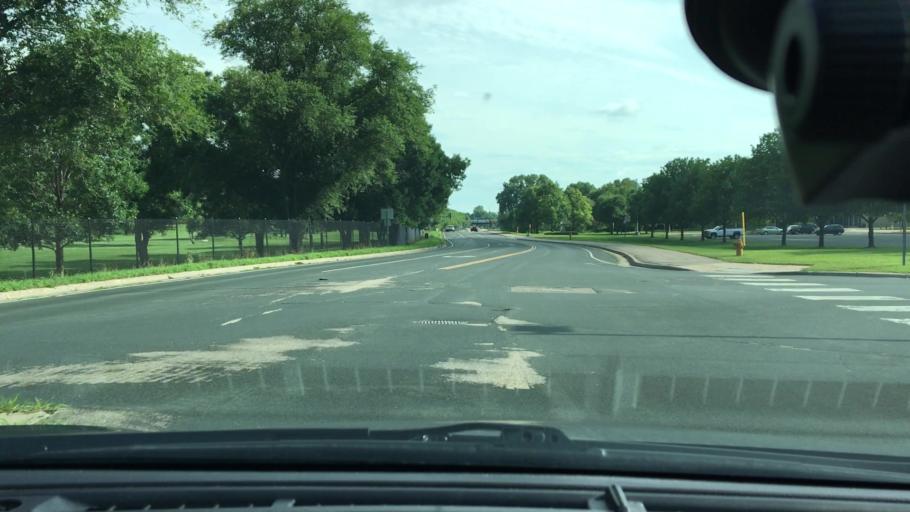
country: US
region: Minnesota
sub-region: Hennepin County
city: Golden Valley
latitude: 44.9820
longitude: -93.3904
